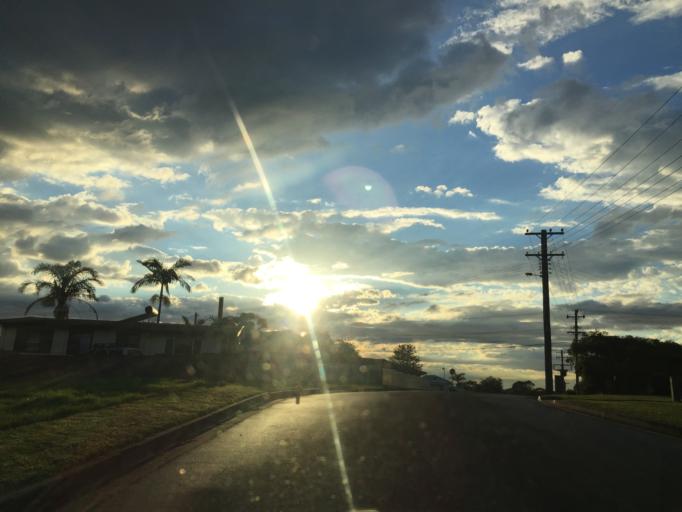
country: AU
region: New South Wales
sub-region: Shellharbour
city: Barrack Heights
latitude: -34.5621
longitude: 150.8510
